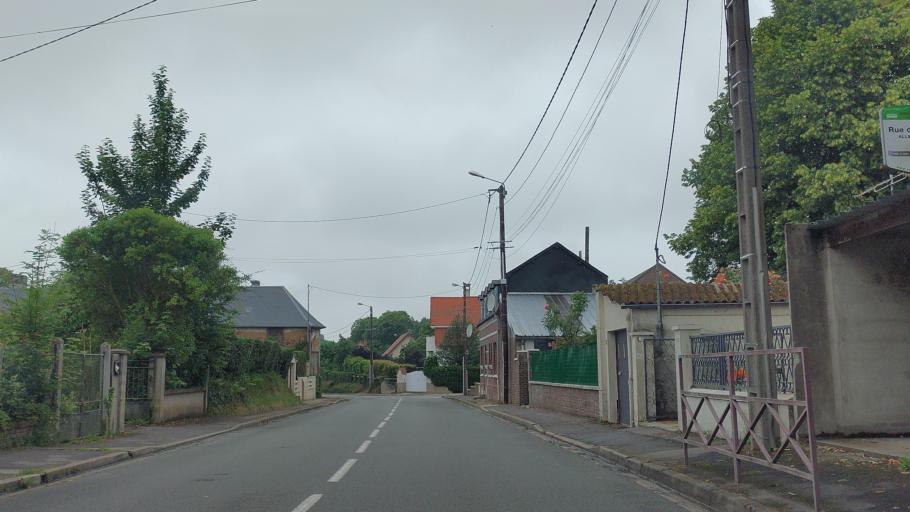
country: FR
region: Picardie
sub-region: Departement de la Somme
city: Bethencourt-sur-Mer
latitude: 50.0862
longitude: 1.4913
